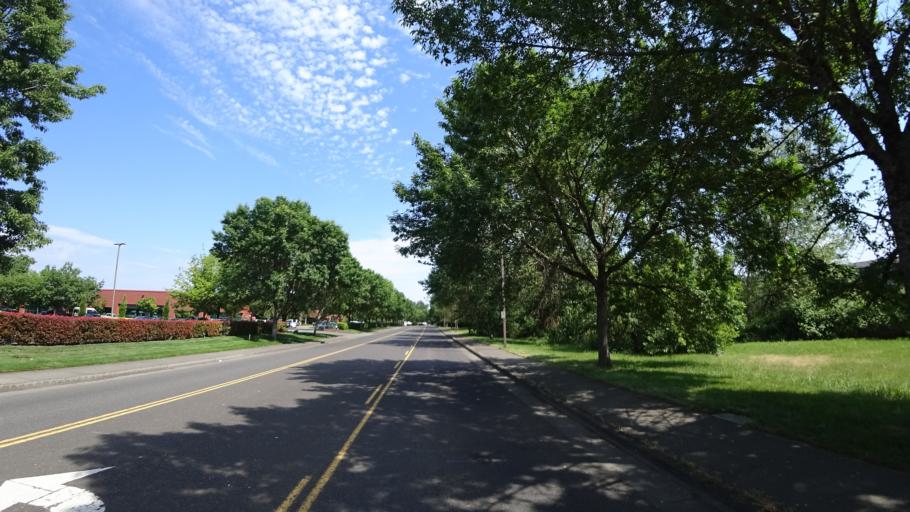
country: US
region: Washington
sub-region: Clark County
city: Mill Plain
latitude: 45.5700
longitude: -122.5431
